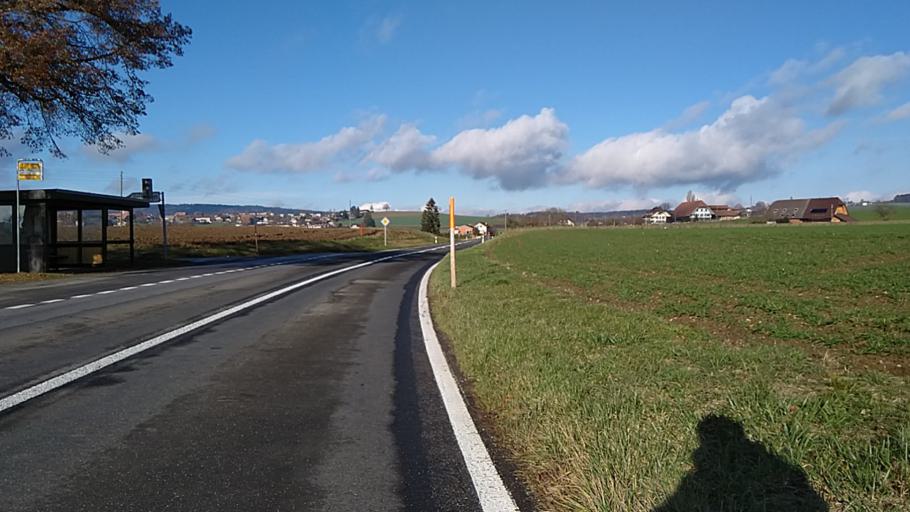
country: CH
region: Bern
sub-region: Bern-Mittelland District
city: Kirchlindach
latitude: 46.9792
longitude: 7.4007
